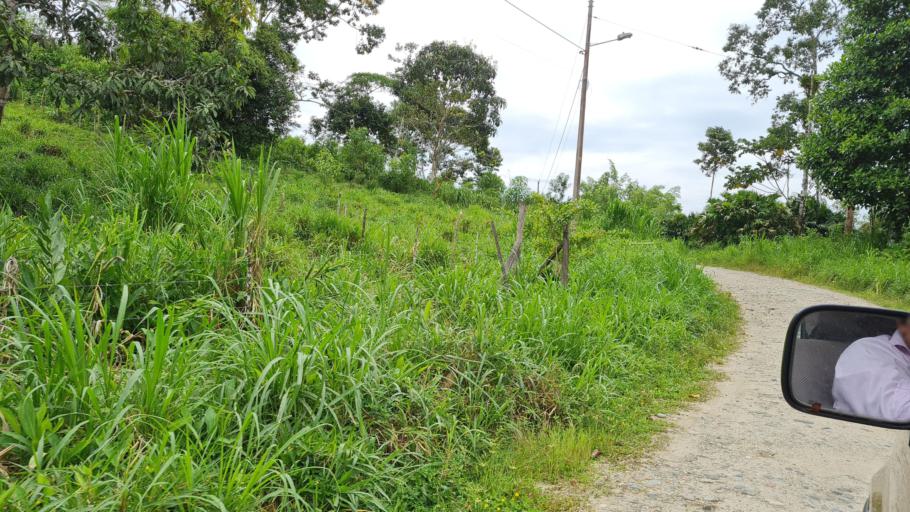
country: EC
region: Napo
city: Tena
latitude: -1.0017
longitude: -77.7664
